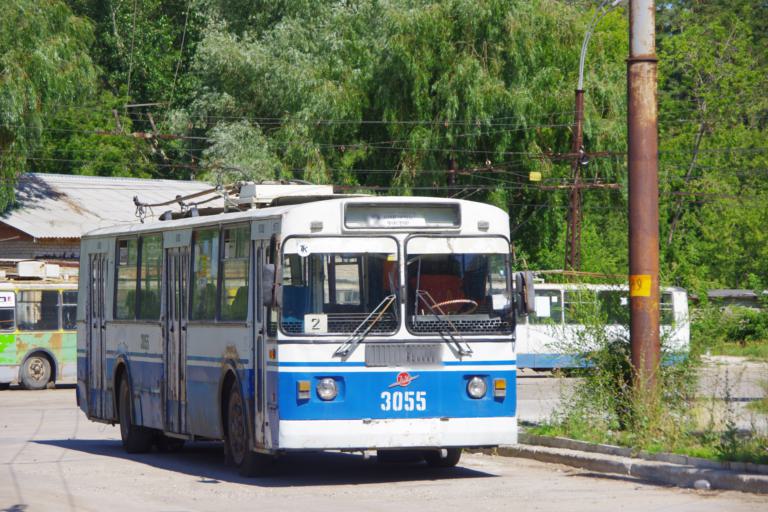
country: RU
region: Samara
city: Tol'yatti
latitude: 53.5048
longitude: 49.3904
